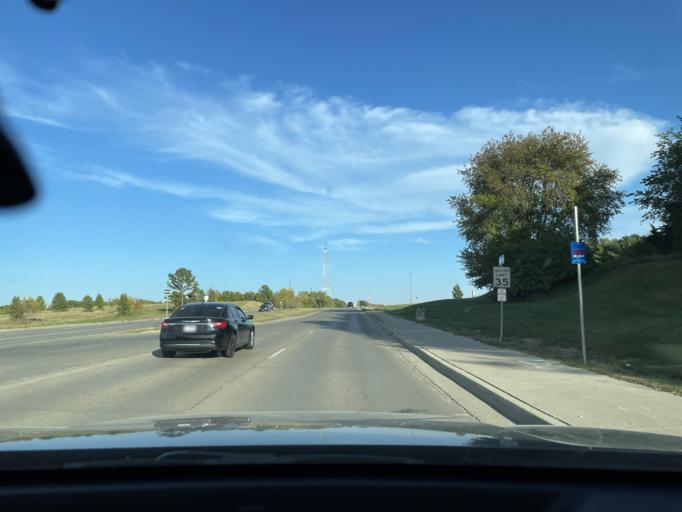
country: US
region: Missouri
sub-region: Buchanan County
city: Saint Joseph
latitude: 39.7696
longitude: -94.8119
